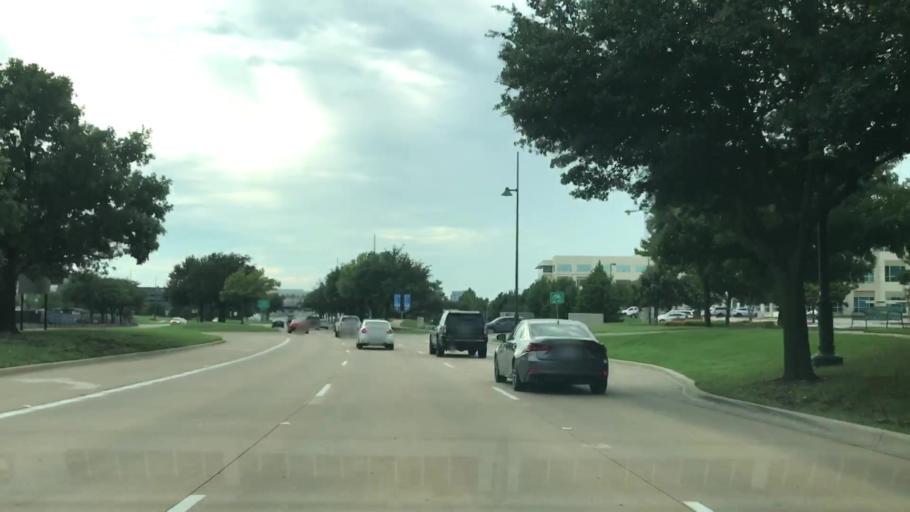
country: US
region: Texas
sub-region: Collin County
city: Frisco
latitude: 33.1071
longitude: -96.8185
